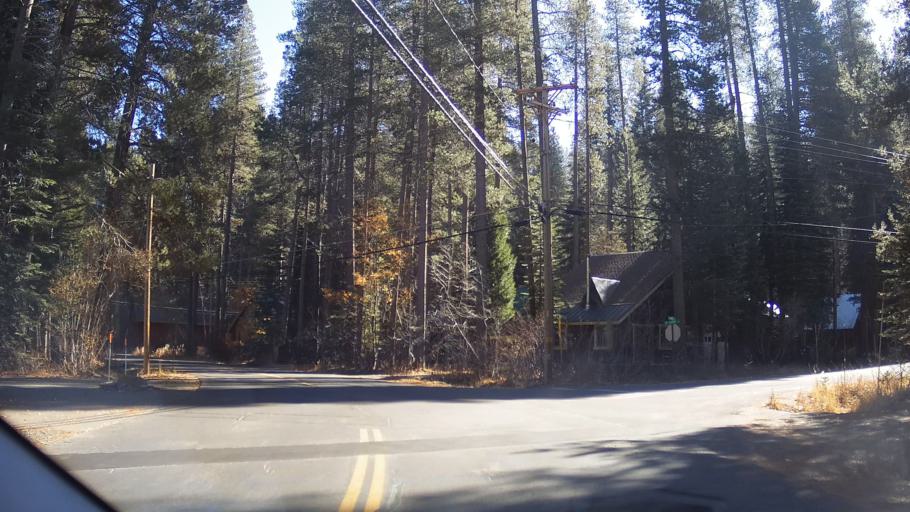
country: US
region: California
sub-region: Nevada County
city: Truckee
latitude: 39.3175
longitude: -120.2888
